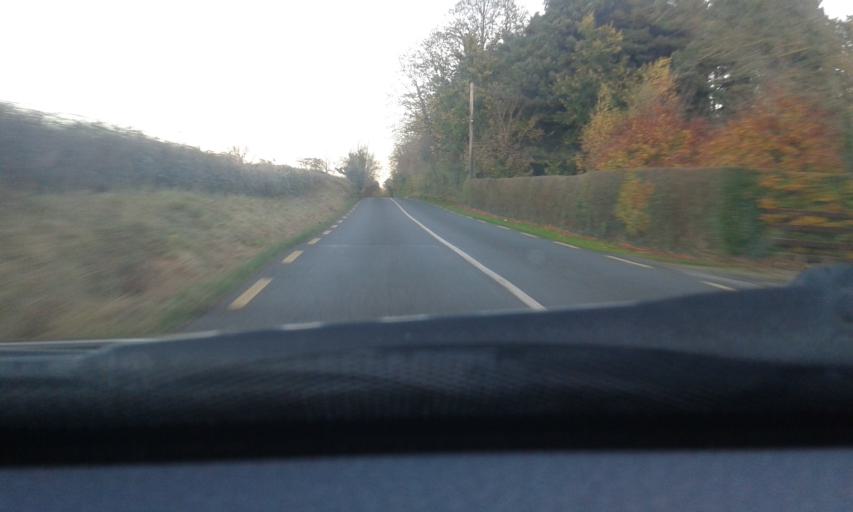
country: IE
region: Leinster
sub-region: Kildare
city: Rathangan
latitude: 53.1879
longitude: -7.0139
